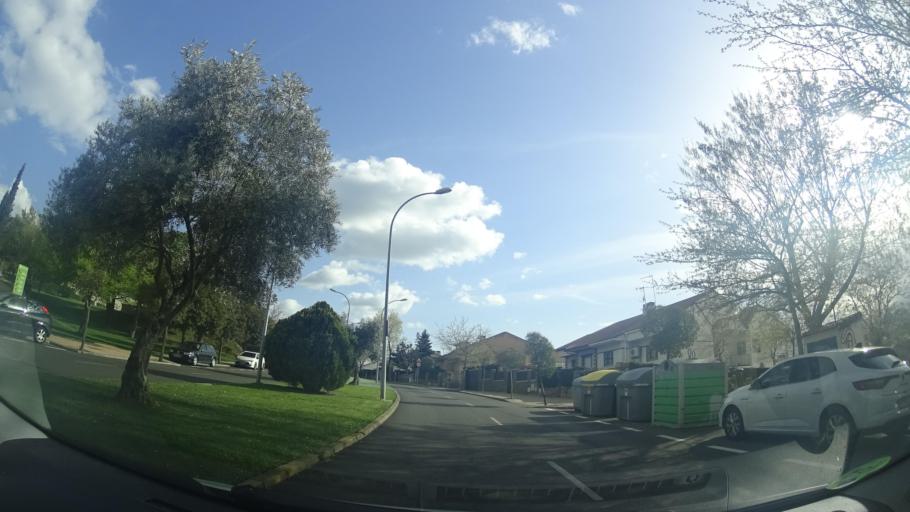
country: ES
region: Madrid
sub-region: Provincia de Madrid
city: Colmenar Viejo
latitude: 40.6611
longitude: -3.7765
